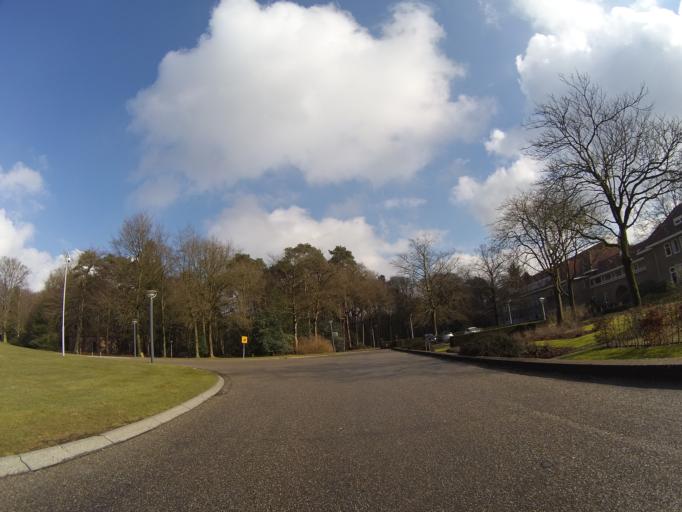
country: NL
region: Utrecht
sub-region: Gemeente Amersfoort
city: Amersfoort
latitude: 52.1346
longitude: 5.3409
